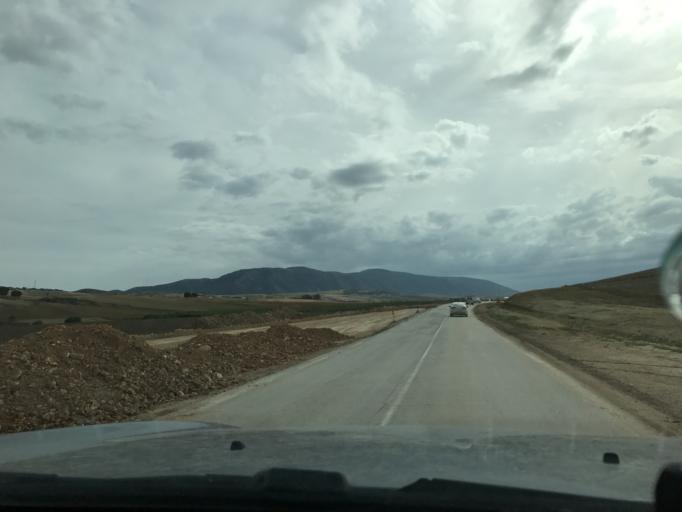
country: TN
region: Silyanah
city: Bu `Aradah
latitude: 36.1560
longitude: 9.6379
